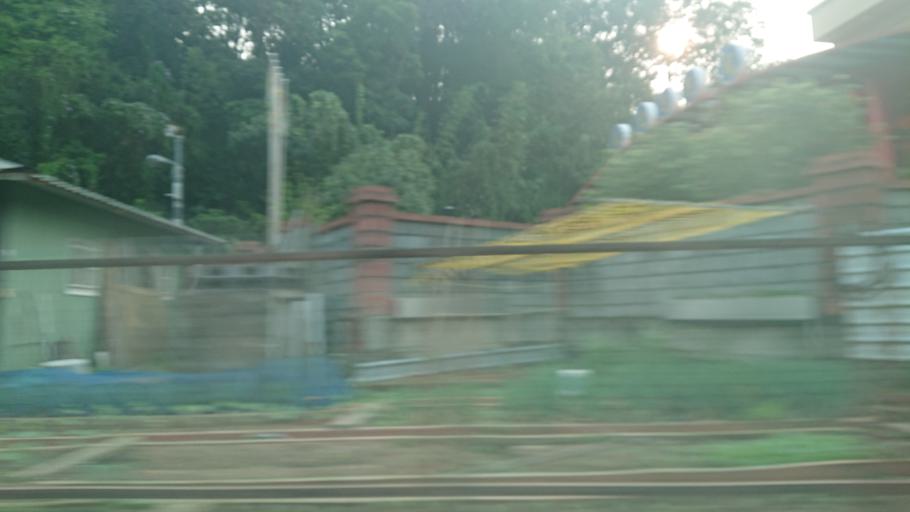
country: TW
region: Taiwan
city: Daxi
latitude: 24.8941
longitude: 121.3754
